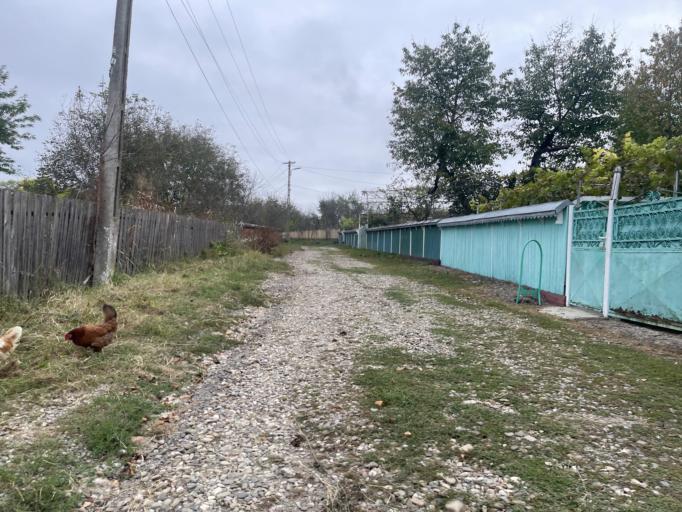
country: RO
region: Iasi
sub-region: Comuna Dumesti
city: Dumesti
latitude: 47.1721
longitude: 27.3448
